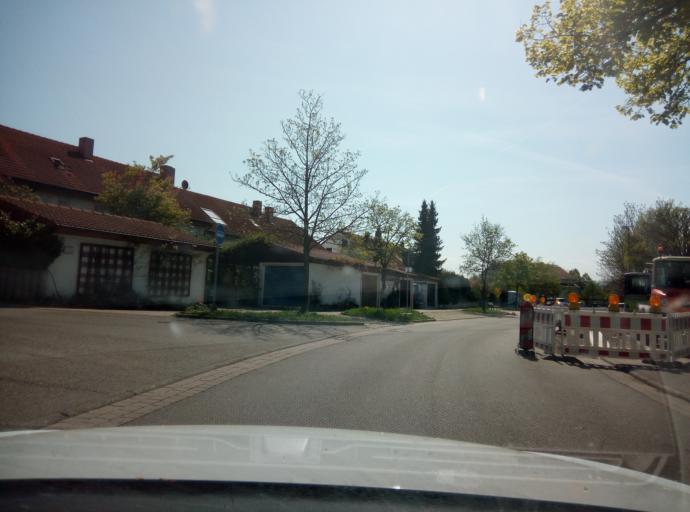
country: DE
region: Baden-Wuerttemberg
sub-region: Tuebingen Region
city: Kusterdingen
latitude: 48.5361
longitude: 9.0925
